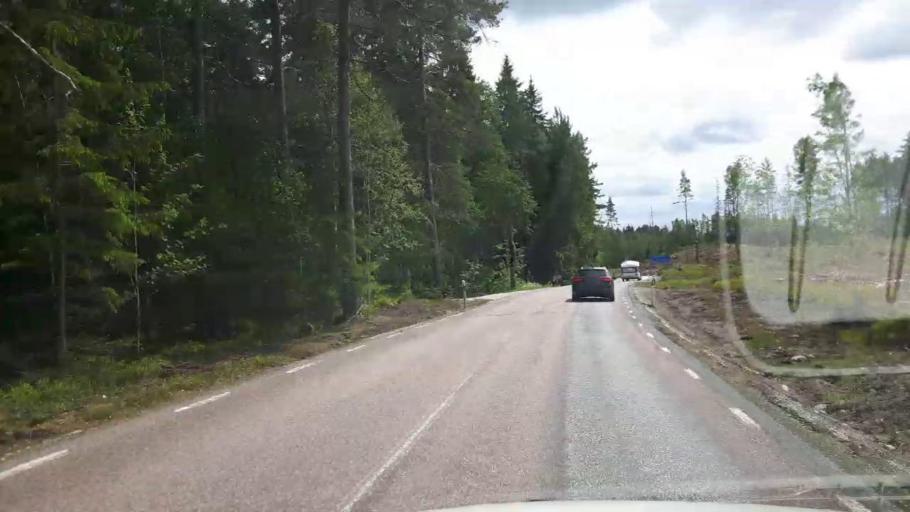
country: SE
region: Vaestmanland
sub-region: Skinnskattebergs Kommun
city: Skinnskatteberg
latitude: 59.8058
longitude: 15.8421
